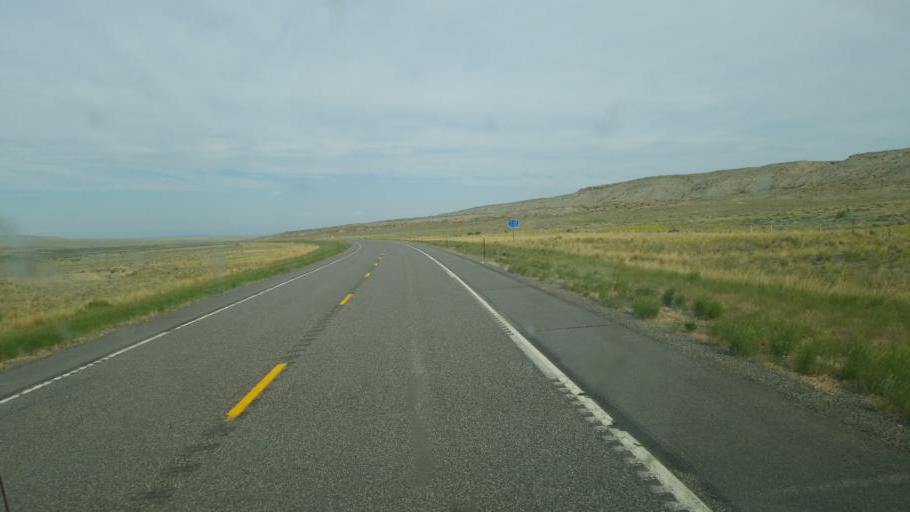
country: US
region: Wyoming
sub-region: Fremont County
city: Riverton
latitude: 43.2219
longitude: -107.9759
